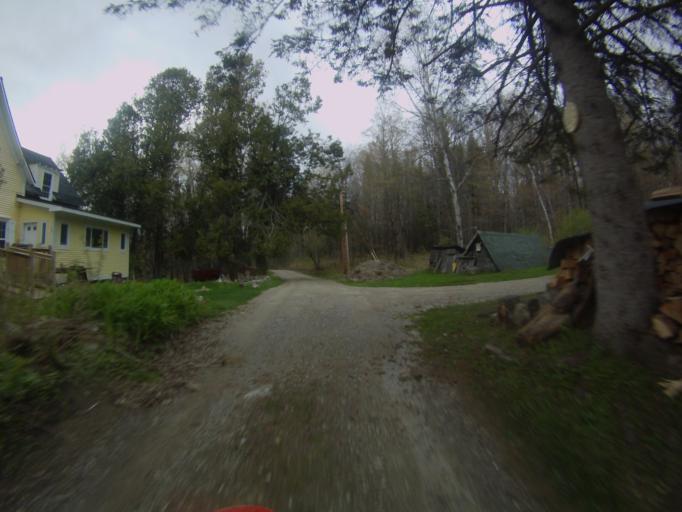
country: US
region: Vermont
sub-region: Addison County
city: Bristol
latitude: 44.0629
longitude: -73.0493
